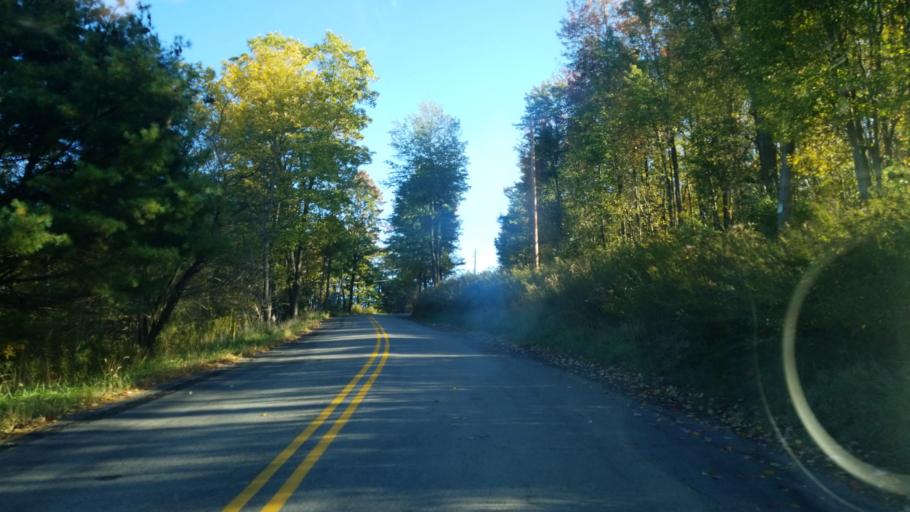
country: US
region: Pennsylvania
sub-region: Indiana County
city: Johnsonburg
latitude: 40.9073
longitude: -78.8781
